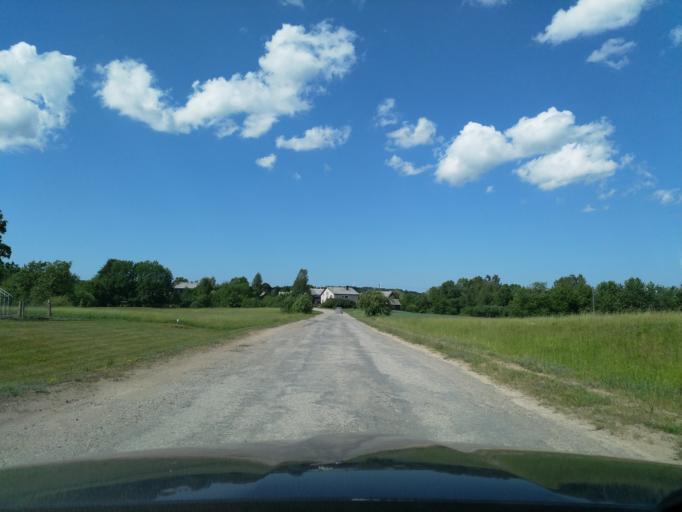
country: LV
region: Alsunga
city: Alsunga
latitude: 56.9714
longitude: 21.5688
